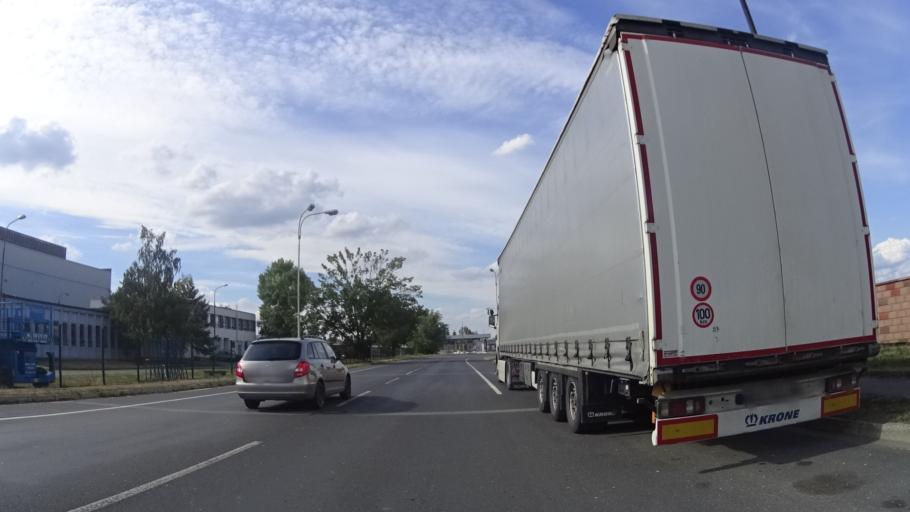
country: CZ
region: Olomoucky
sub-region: Okres Sumperk
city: Mohelnice
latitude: 49.7765
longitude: 16.9405
